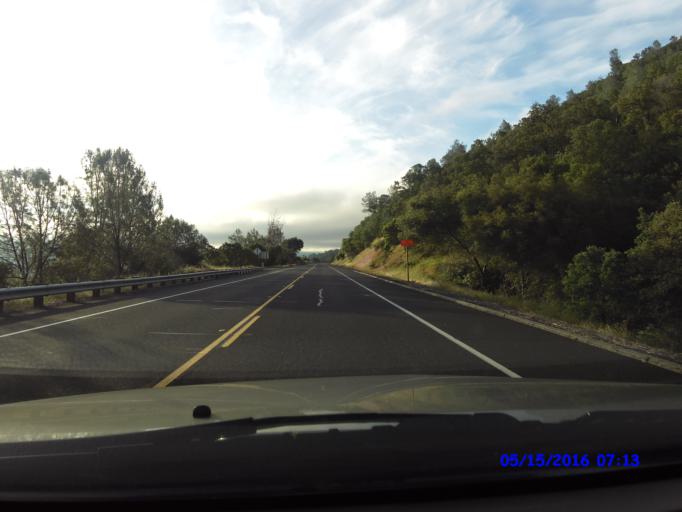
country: US
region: California
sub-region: Tuolumne County
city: Jamestown
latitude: 37.8392
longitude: -120.3670
